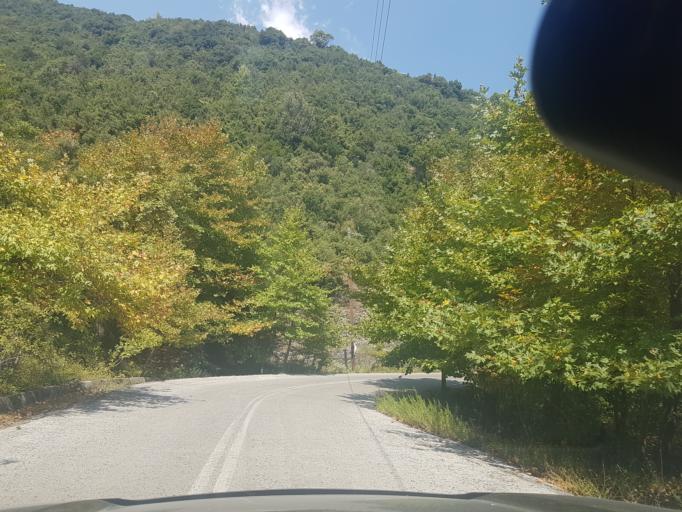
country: GR
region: Central Greece
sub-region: Nomos Evvoias
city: Yimnon
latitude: 38.6359
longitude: 23.8908
